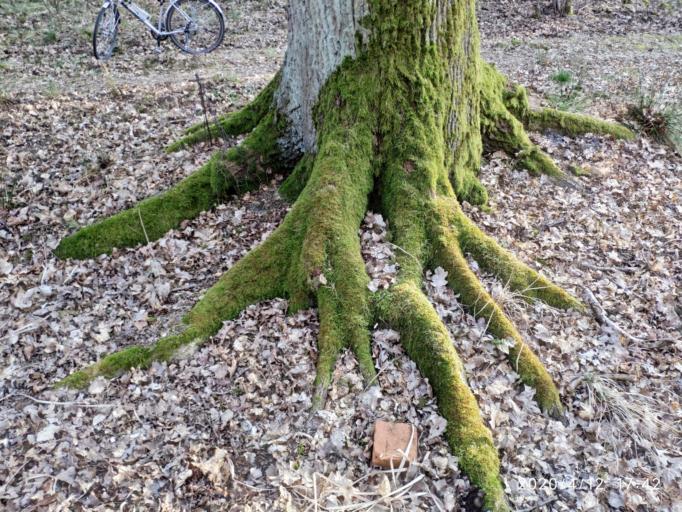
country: PL
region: Lubusz
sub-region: Powiat krosnienski
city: Dabie
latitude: 52.0413
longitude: 15.2217
